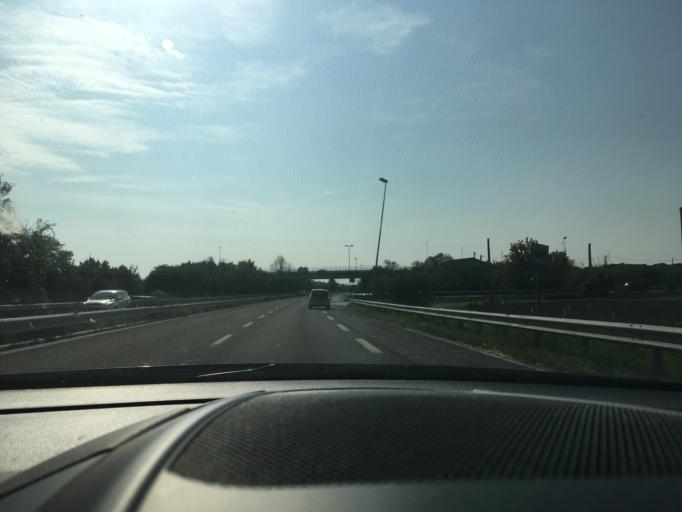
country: IT
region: Emilia-Romagna
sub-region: Provincia di Rimini
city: Bellaria-Igea Marina
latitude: 44.1435
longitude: 12.4558
